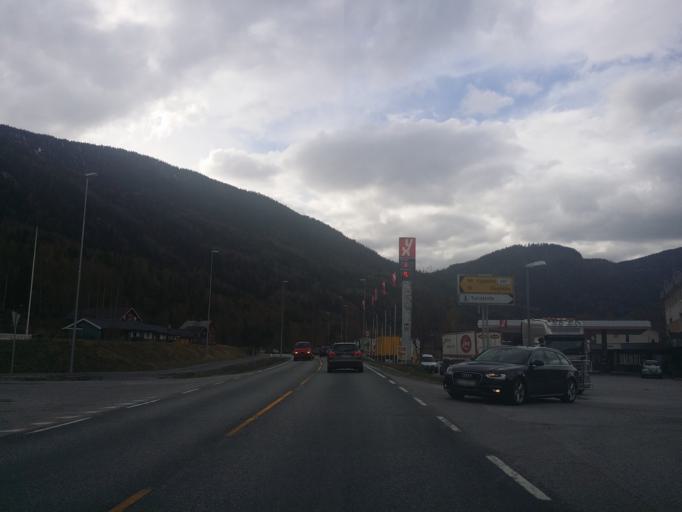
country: NO
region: Buskerud
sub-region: Nes
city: Nesbyen
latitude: 60.4874
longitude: 9.1917
